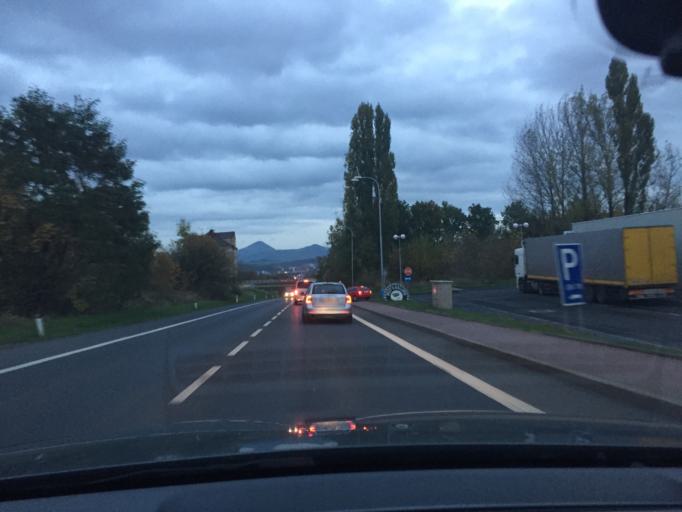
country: CZ
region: Ustecky
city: Novosedlice
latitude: 50.6549
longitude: 13.8071
